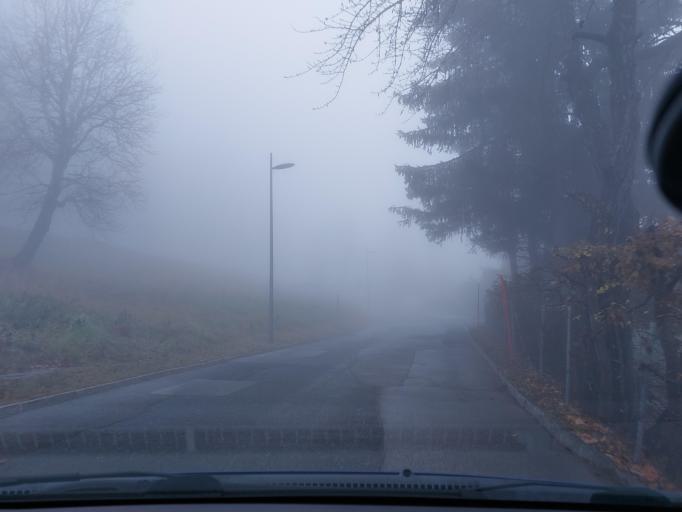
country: CH
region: Valais
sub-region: Sierre District
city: Randogne
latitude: 46.3156
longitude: 7.4942
